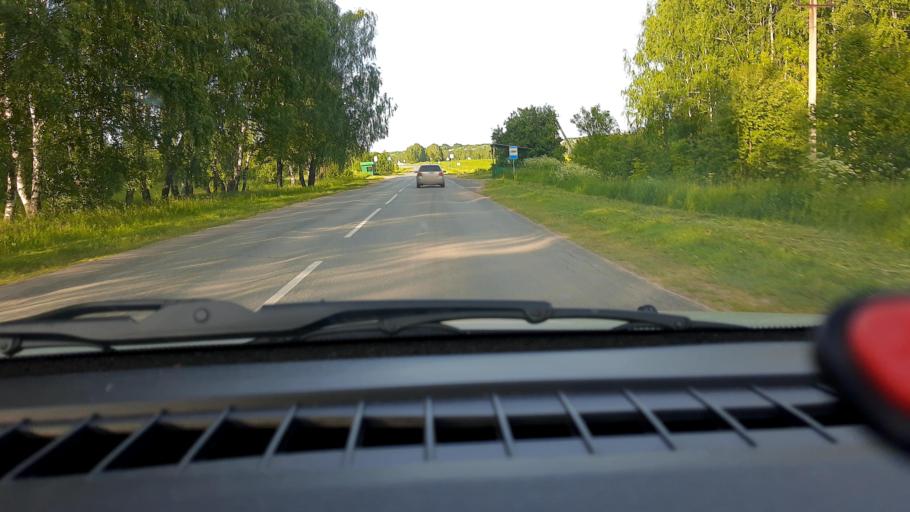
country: RU
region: Nizjnij Novgorod
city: Afonino
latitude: 56.1215
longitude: 43.9998
